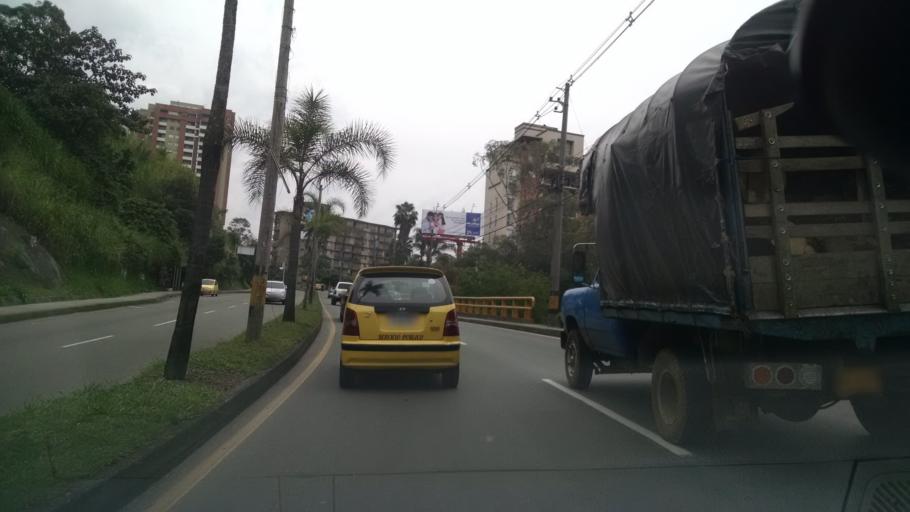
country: CO
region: Antioquia
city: Medellin
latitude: 6.2299
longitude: -75.5665
